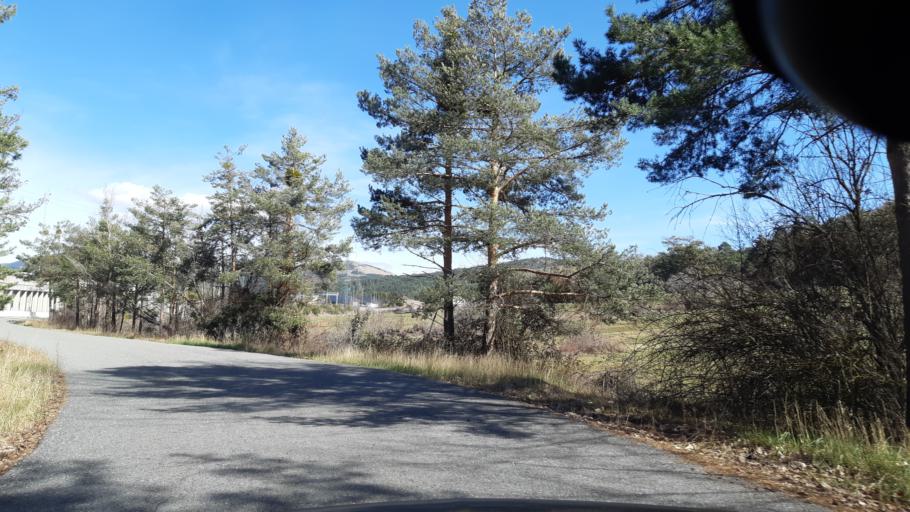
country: ES
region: Madrid
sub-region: Provincia de Madrid
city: Guadarrama
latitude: 40.7126
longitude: -4.1695
